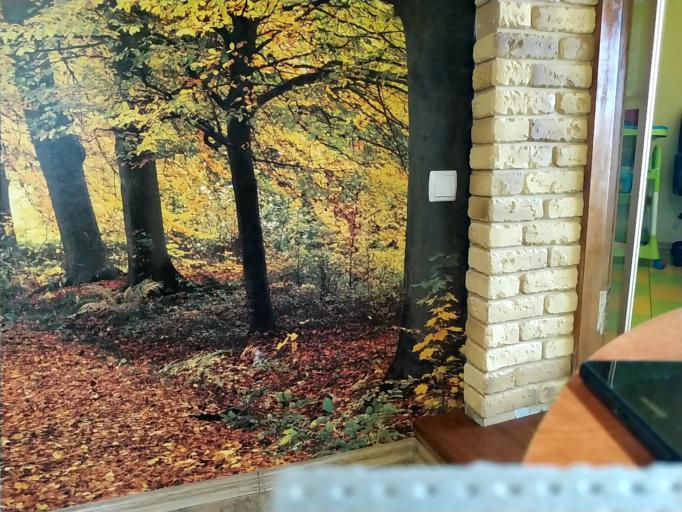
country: RU
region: Kaluga
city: Nikola-Lenivets
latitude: 54.8538
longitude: 35.4588
